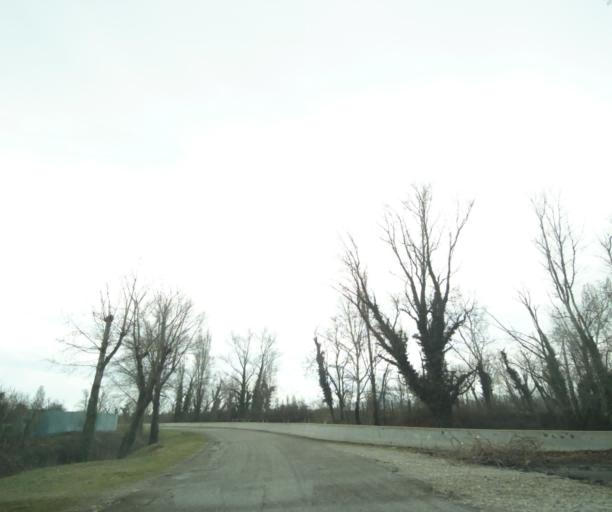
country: FR
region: Rhone-Alpes
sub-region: Departement de l'Ardeche
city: Cornas
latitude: 44.9748
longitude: 4.8614
